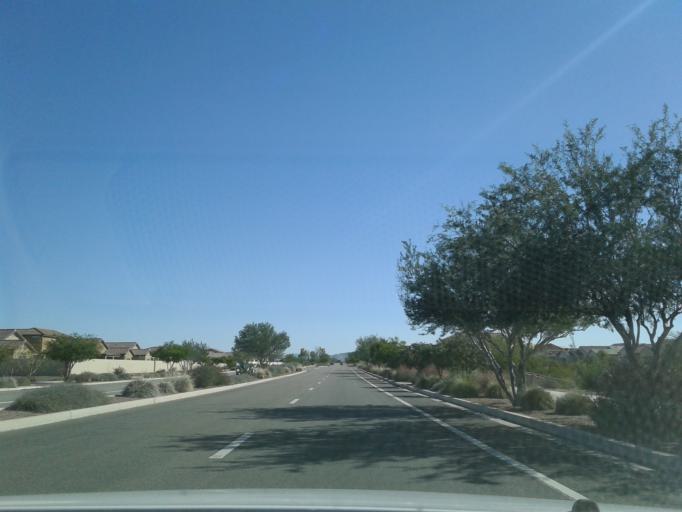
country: US
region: Arizona
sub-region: Pima County
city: Avra Valley
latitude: 32.5688
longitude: -111.3406
